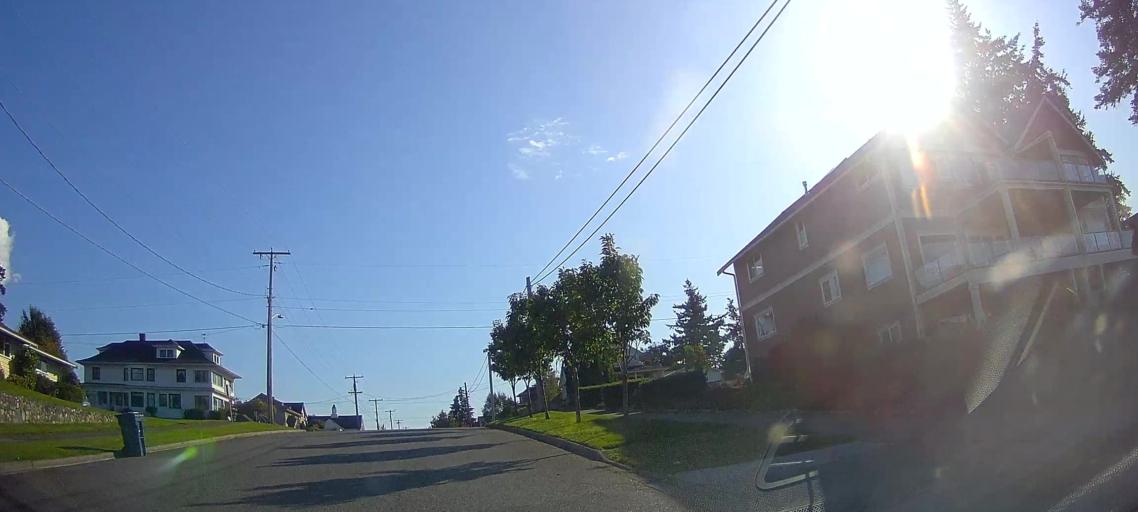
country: US
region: Washington
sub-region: Skagit County
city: Anacortes
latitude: 48.5172
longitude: -122.6204
